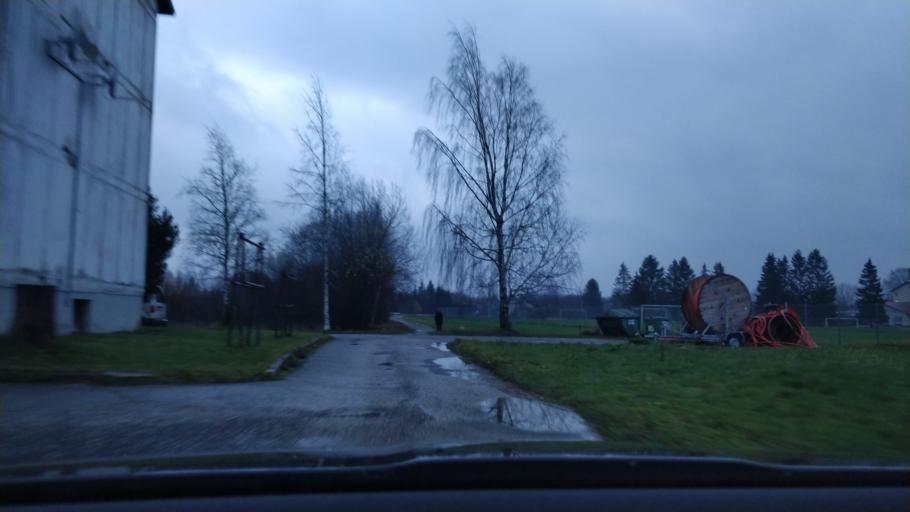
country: EE
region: Laeaene
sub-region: Lihula vald
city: Lihula
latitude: 58.6878
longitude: 23.8389
